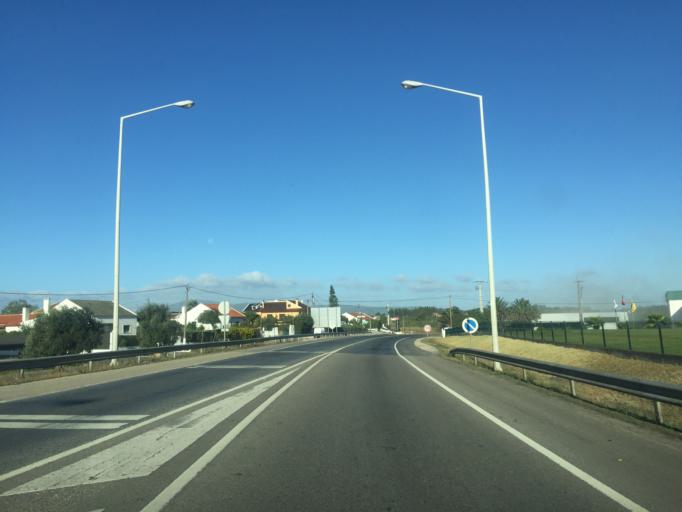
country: PT
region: Lisbon
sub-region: Azambuja
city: Aveiras de Cima
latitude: 39.1457
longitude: -8.9030
